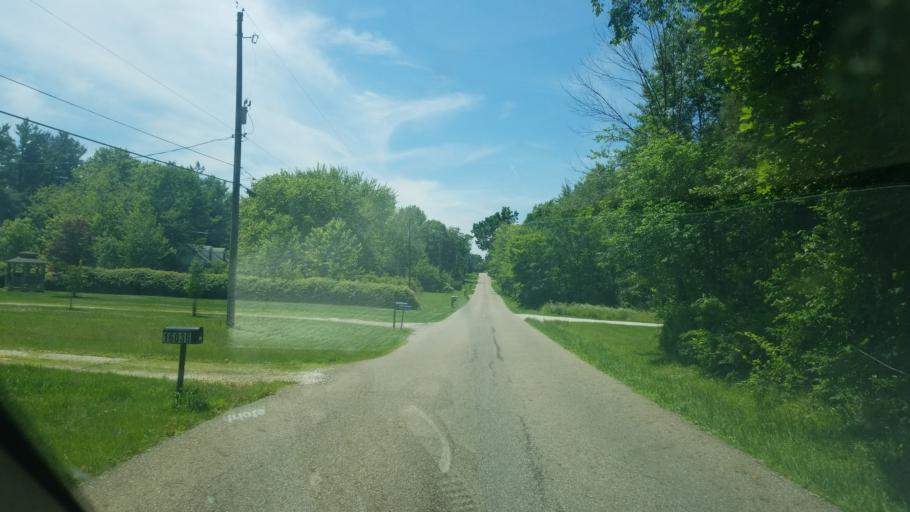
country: US
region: Ohio
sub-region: Stark County
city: Alliance
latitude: 40.8575
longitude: -81.0974
